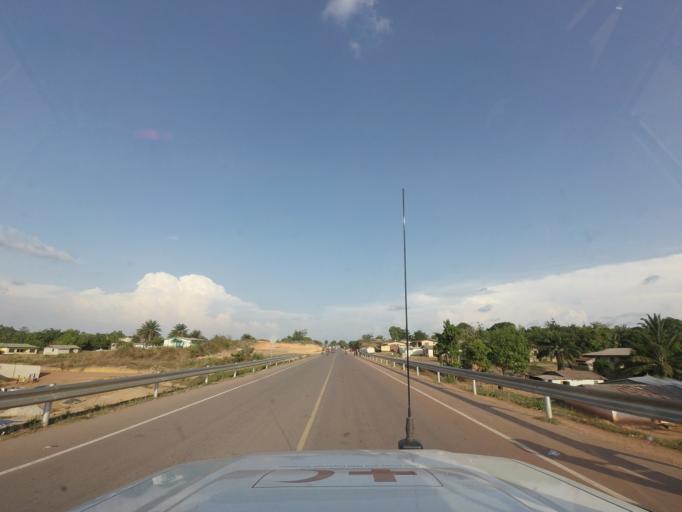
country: LR
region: Bong
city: Gbarnga
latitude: 6.9937
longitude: -9.4623
